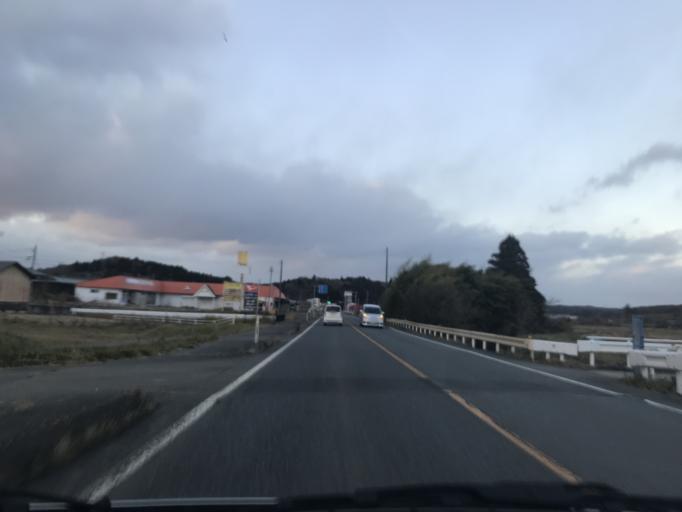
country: JP
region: Iwate
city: Ichinoseki
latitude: 38.8125
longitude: 141.0775
